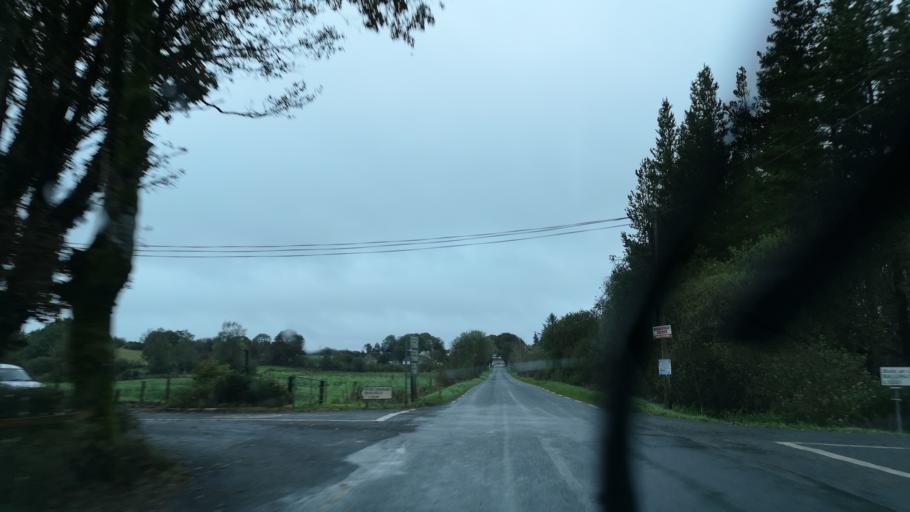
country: IE
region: Connaught
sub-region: Maigh Eo
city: Ballyhaunis
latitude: 53.8044
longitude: -8.6810
